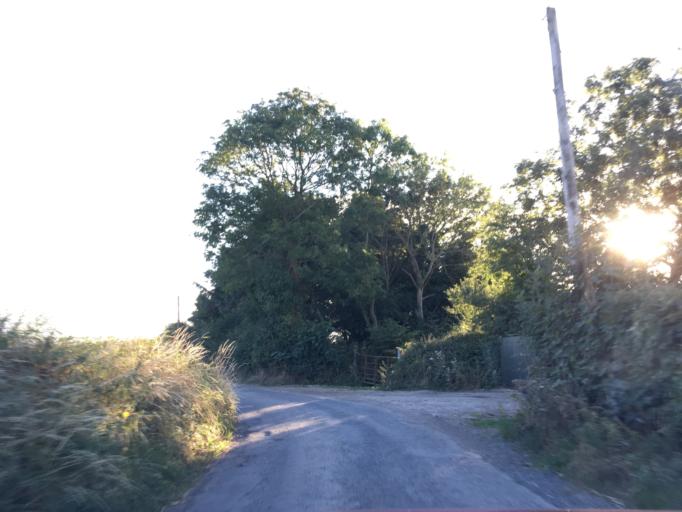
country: IE
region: Munster
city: Cashel
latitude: 52.4916
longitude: -7.9474
